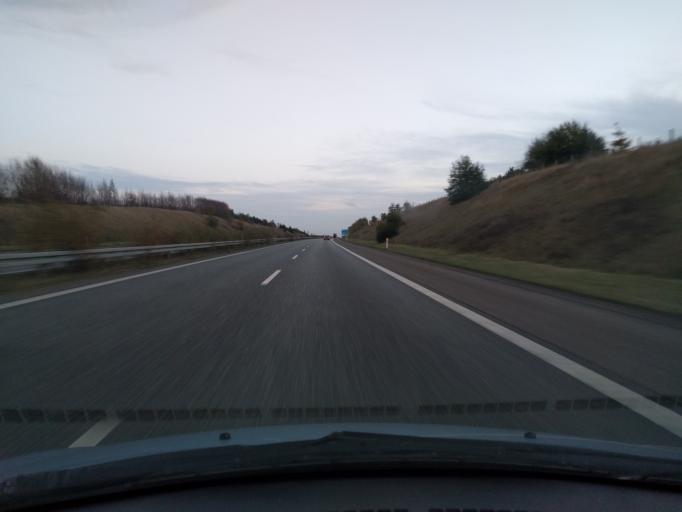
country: DK
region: South Denmark
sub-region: Faaborg-Midtfyn Kommune
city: Arslev
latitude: 55.2771
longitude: 10.4590
